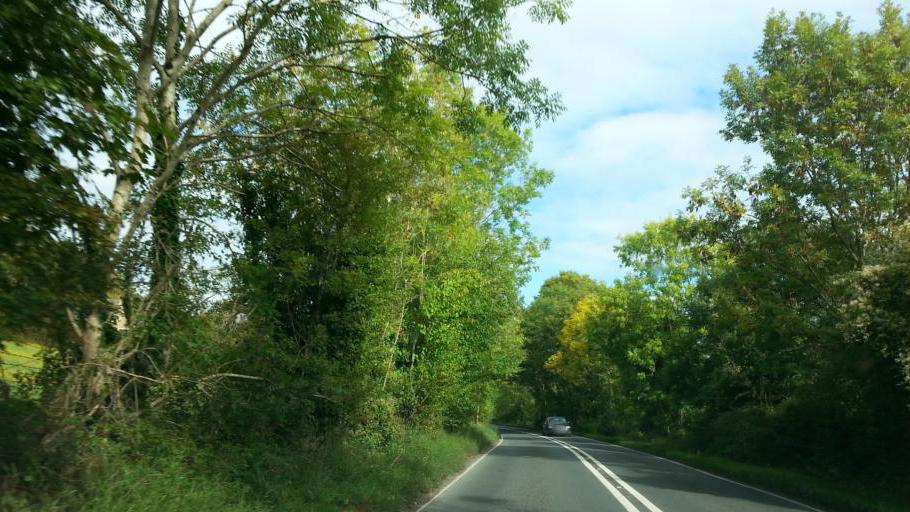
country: GB
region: England
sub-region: Gloucestershire
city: Painswick
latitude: 51.8055
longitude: -2.1875
